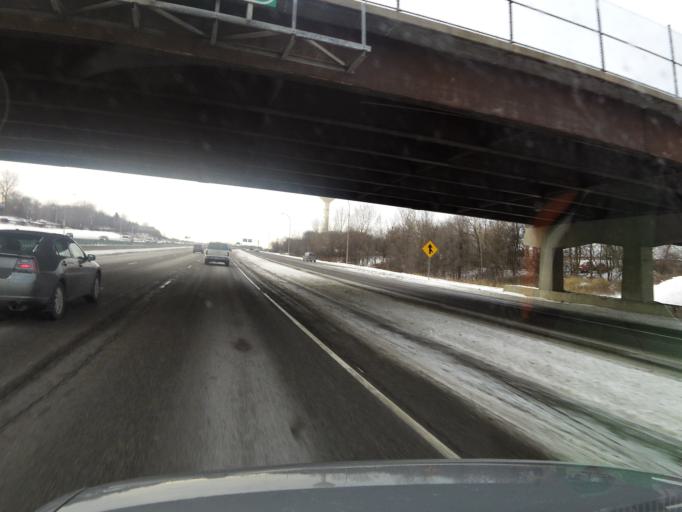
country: US
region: Minnesota
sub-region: Dakota County
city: South Saint Paul
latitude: 44.8750
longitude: -93.0642
